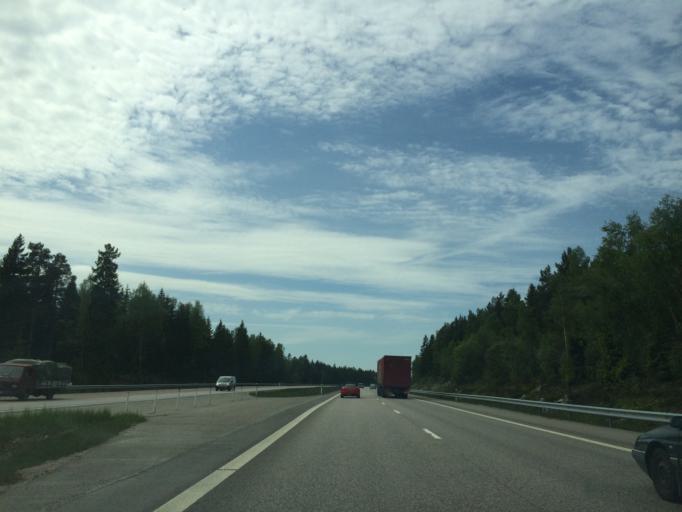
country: SE
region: Soedermanland
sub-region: Trosa Kommun
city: Vagnharad
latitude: 58.9270
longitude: 17.3952
